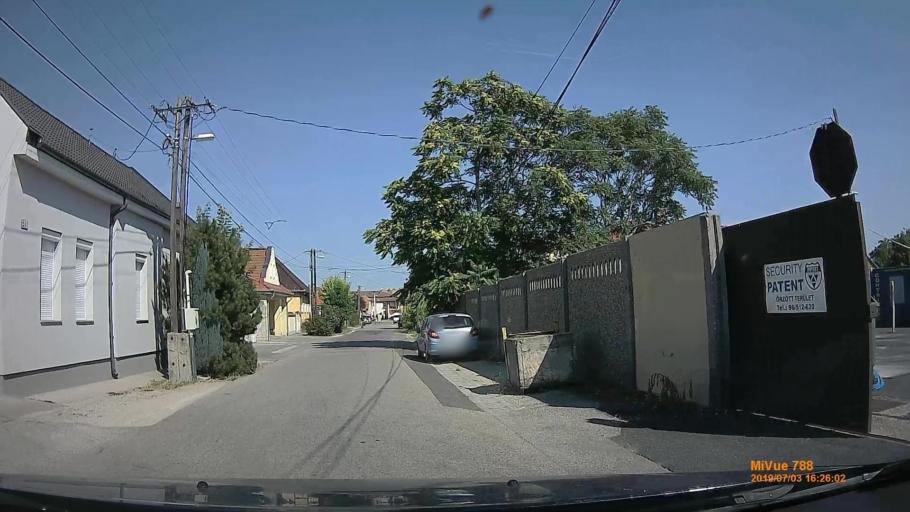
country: HU
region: Gyor-Moson-Sopron
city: Gyor
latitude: 47.6847
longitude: 17.6108
